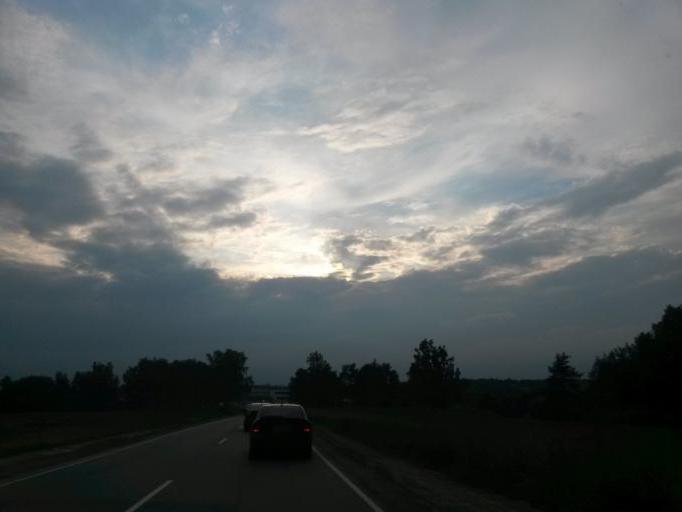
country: RU
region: Moskovskaya
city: Vostryakovo
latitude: 55.3534
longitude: 37.7486
